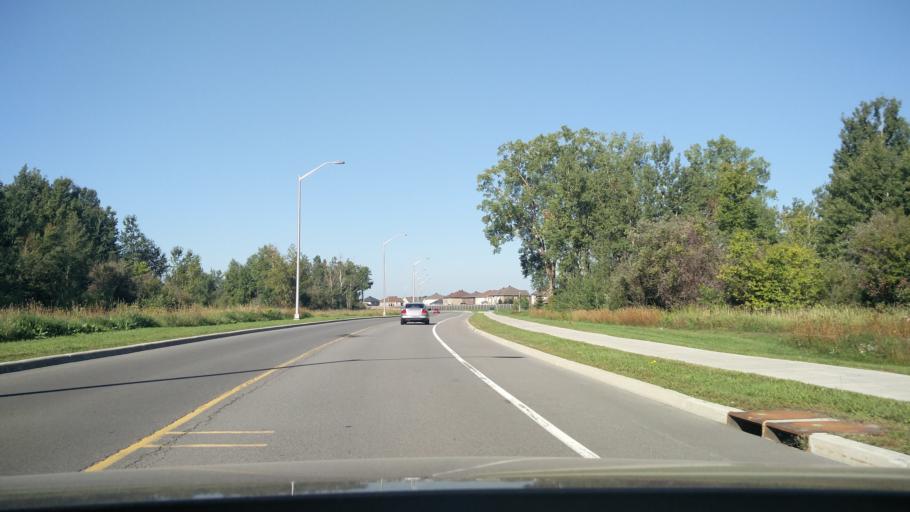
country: CA
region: Ontario
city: Clarence-Rockland
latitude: 45.4571
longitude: -75.4499
